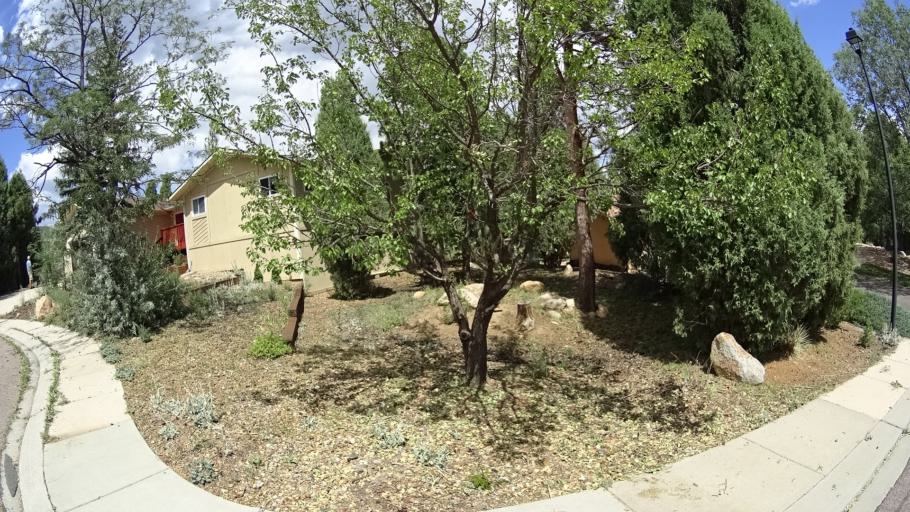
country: US
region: Colorado
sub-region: El Paso County
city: Stratmoor
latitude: 38.7714
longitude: -104.8213
